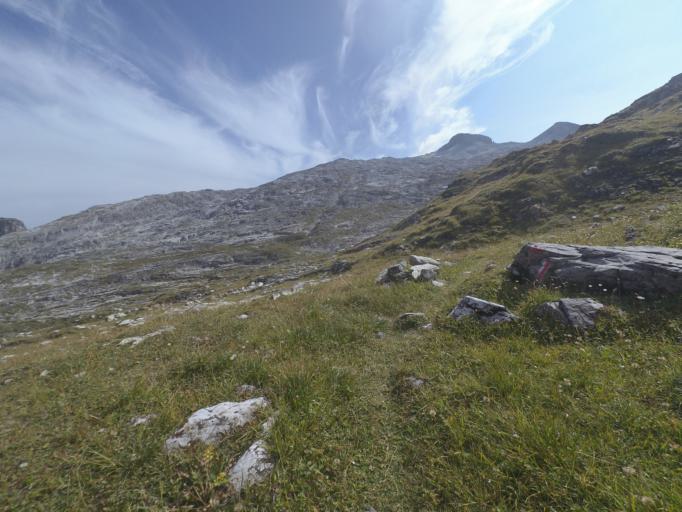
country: AT
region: Salzburg
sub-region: Politischer Bezirk Sankt Johann im Pongau
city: Kleinarl
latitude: 47.2265
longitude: 13.3930
